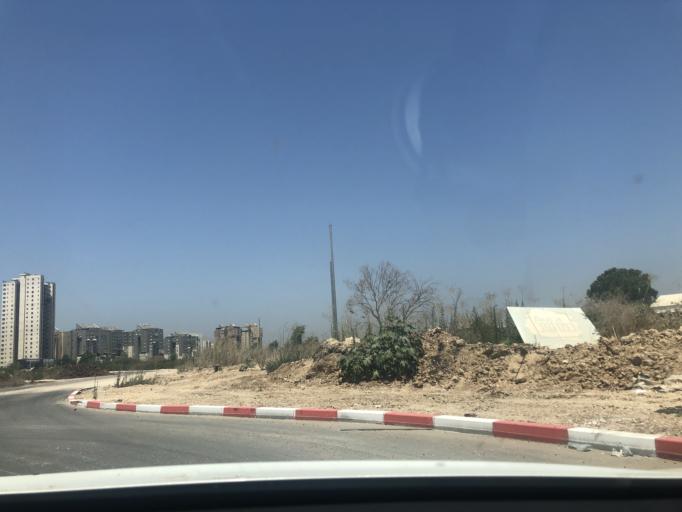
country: IL
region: Central District
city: Lod
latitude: 31.9401
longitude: 34.9023
